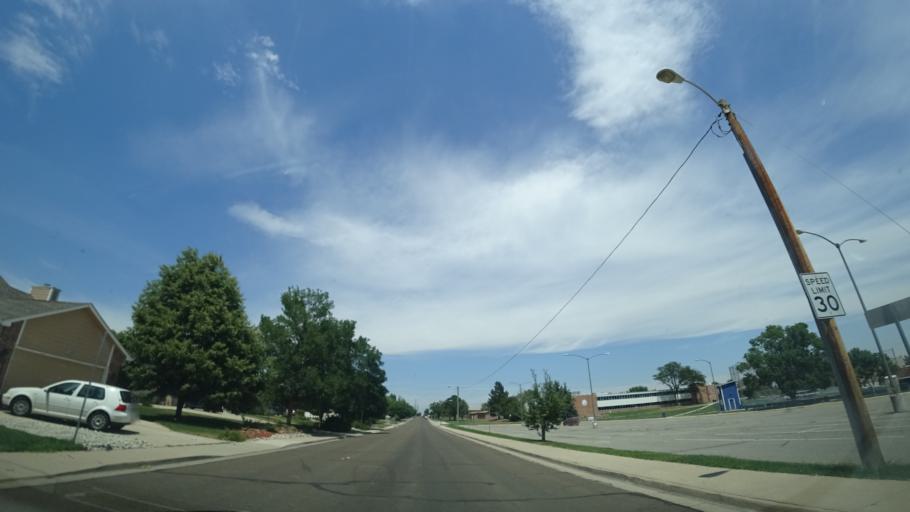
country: US
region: Colorado
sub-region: Jefferson County
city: Lakewood
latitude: 39.6925
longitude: -105.0862
